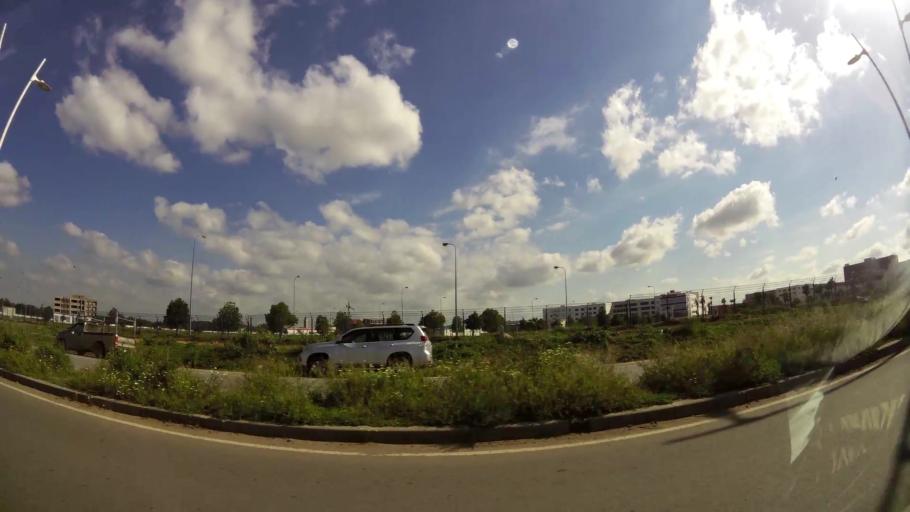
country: MA
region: Grand Casablanca
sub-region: Mediouna
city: Mediouna
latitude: 33.4100
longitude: -7.5366
